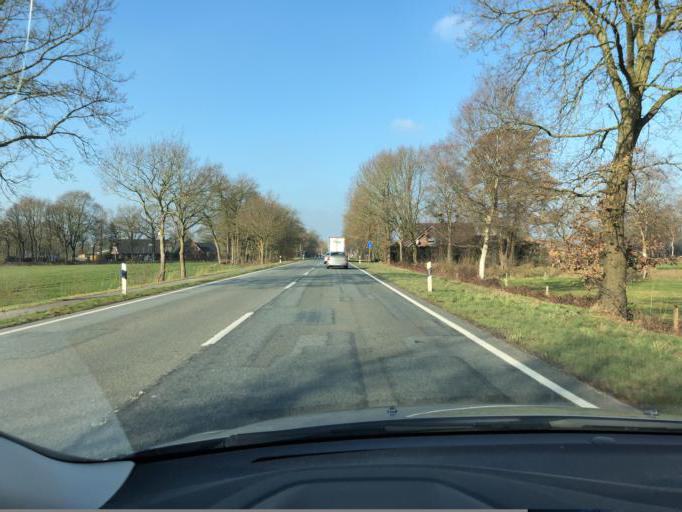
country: DE
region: Lower Saxony
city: Apen
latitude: 53.3030
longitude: 7.7824
